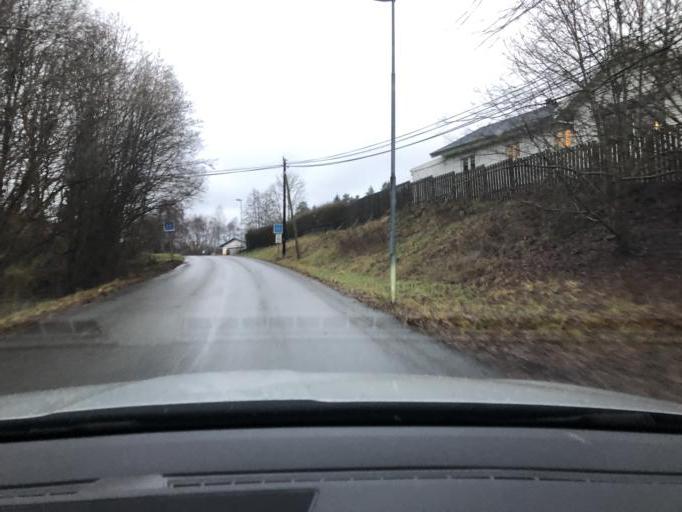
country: SE
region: Vaestra Goetaland
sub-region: Harryda Kommun
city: Landvetter
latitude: 57.6880
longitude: 12.1982
